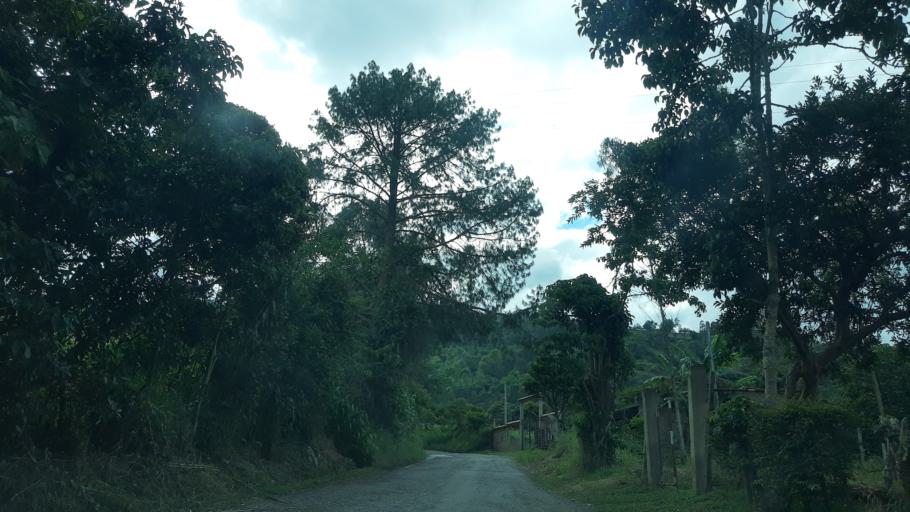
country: CO
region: Cundinamarca
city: Tenza
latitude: 5.0622
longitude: -73.4223
